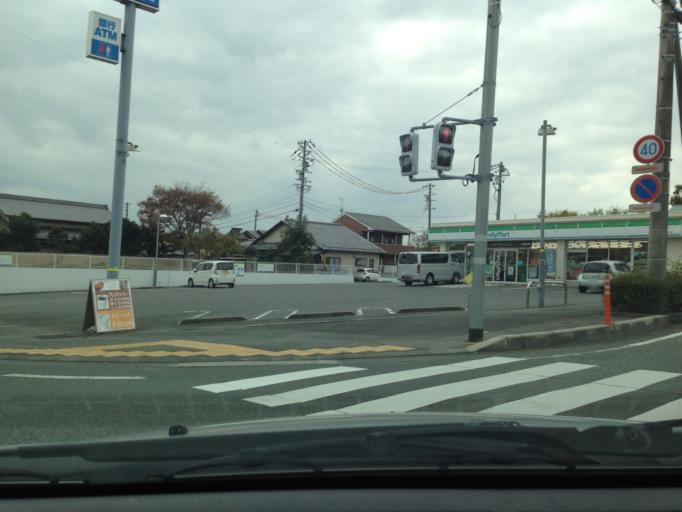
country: JP
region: Shizuoka
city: Fukuroi
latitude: 34.7373
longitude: 137.9378
